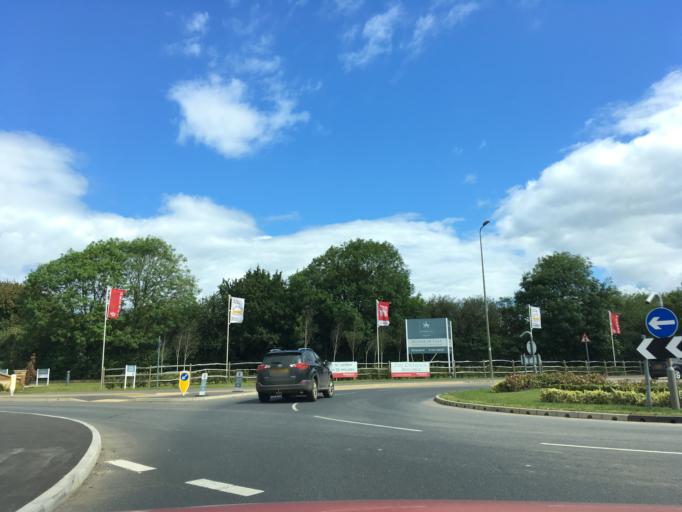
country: GB
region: England
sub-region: Oxfordshire
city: Banbury
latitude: 52.0475
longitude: -1.3544
